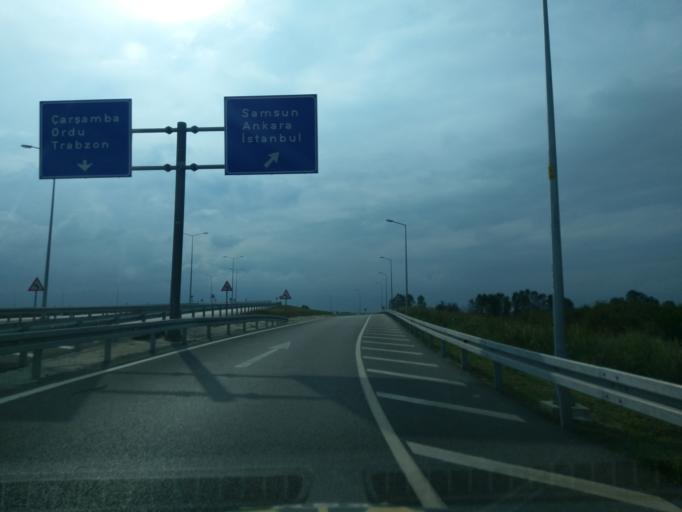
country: TR
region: Samsun
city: Dikbiyik
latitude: 41.2384
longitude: 36.5387
